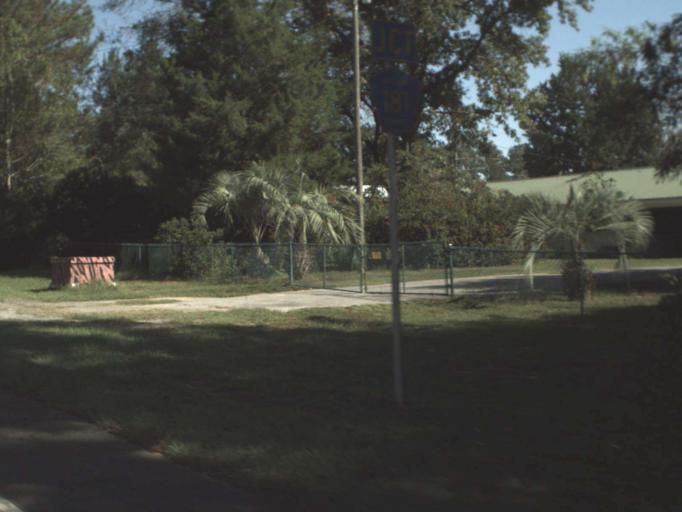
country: US
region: Florida
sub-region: Walton County
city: DeFuniak Springs
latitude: 30.6587
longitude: -85.9365
